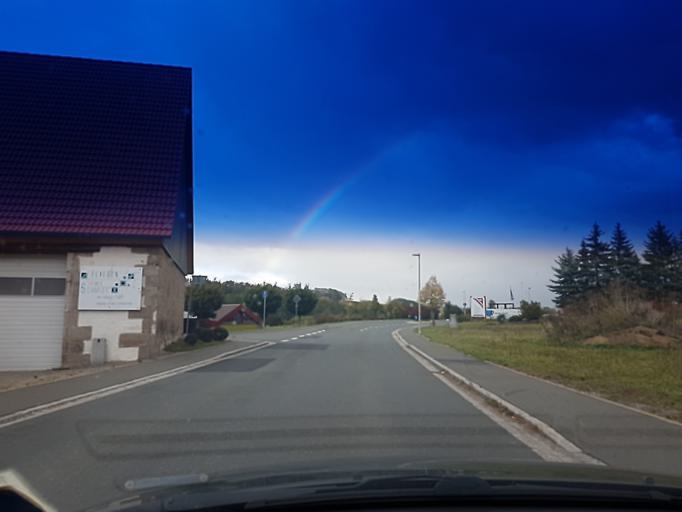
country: DE
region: Bavaria
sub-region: Regierungsbezirk Mittelfranken
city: Burghaslach
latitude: 49.7325
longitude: 10.6195
